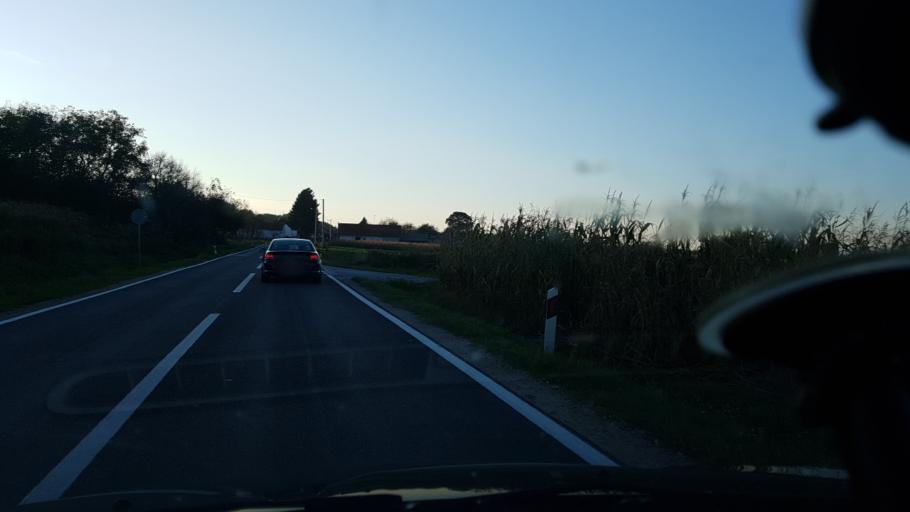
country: HR
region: Koprivnicko-Krizevacka
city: Hlebine
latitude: 46.1050
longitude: 16.9131
